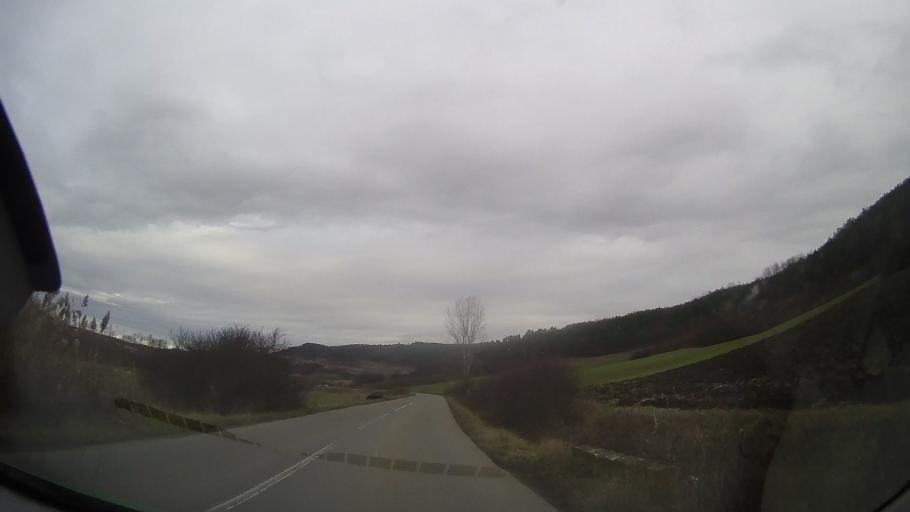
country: RO
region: Mures
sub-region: Comuna Bala
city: Bala
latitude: 46.7286
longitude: 24.5432
